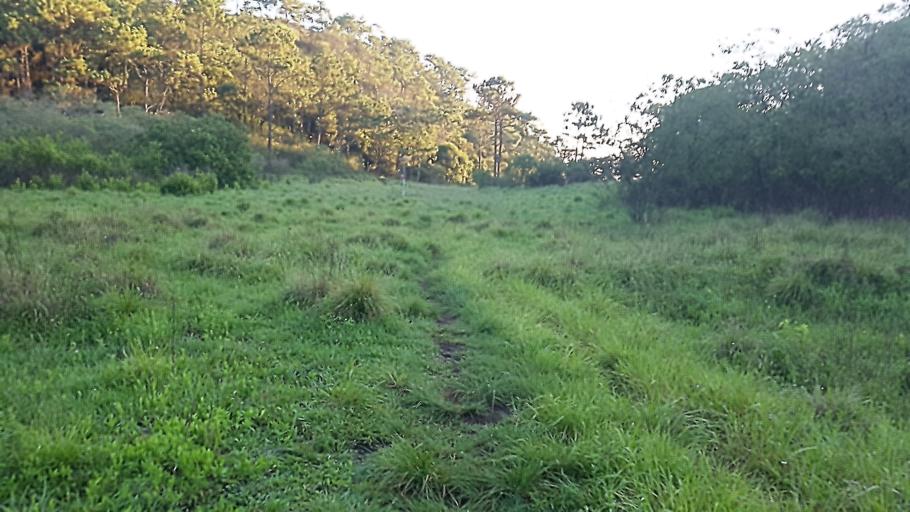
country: MX
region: Nayarit
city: Tepic
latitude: 21.5009
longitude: -104.9307
